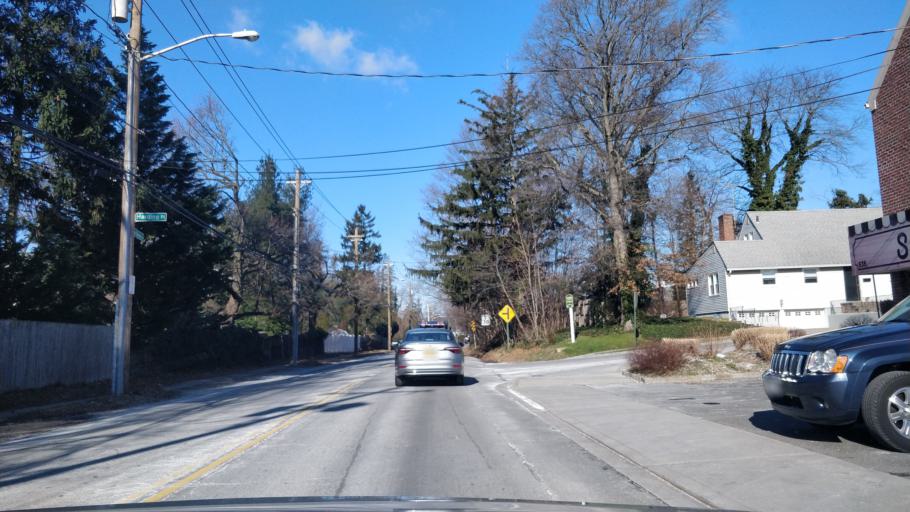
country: US
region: New York
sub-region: Nassau County
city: Glen Head
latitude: 40.8338
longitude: -73.6302
